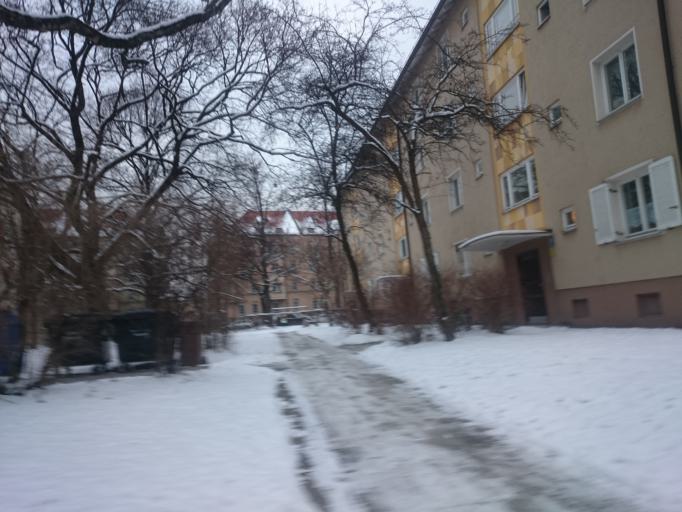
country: DE
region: Bavaria
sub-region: Upper Bavaria
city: Munich
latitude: 48.1562
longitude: 11.5502
